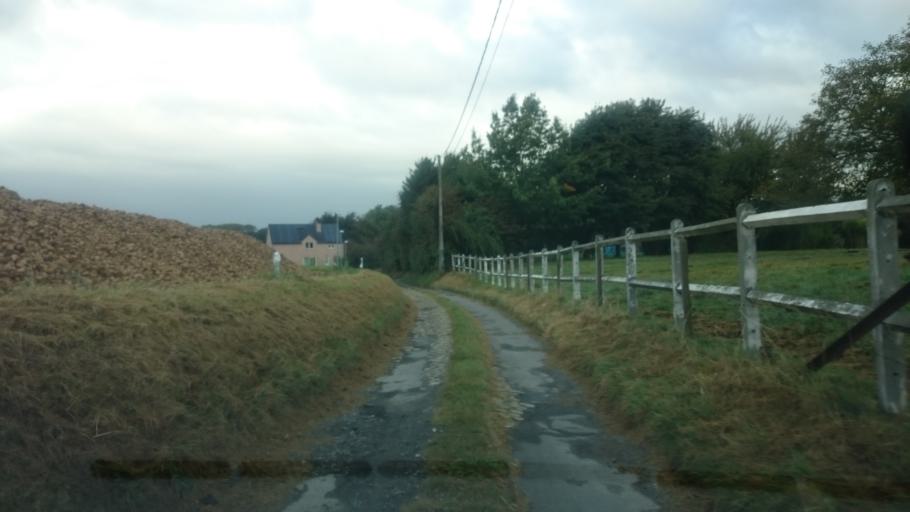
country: BE
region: Wallonia
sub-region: Province du Brabant Wallon
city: Walhain-Saint-Paul
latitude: 50.6617
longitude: 4.6718
